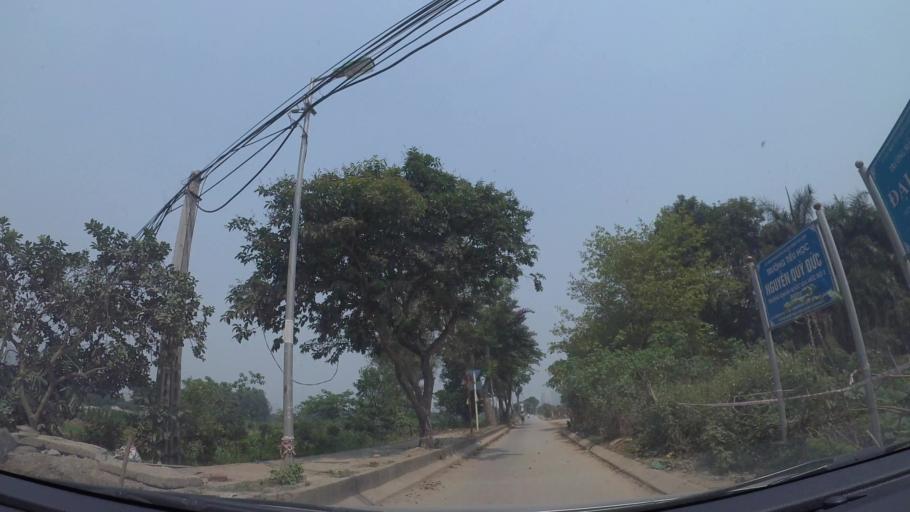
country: VN
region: Ha Noi
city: Ha Dong
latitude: 20.9949
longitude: 105.7619
